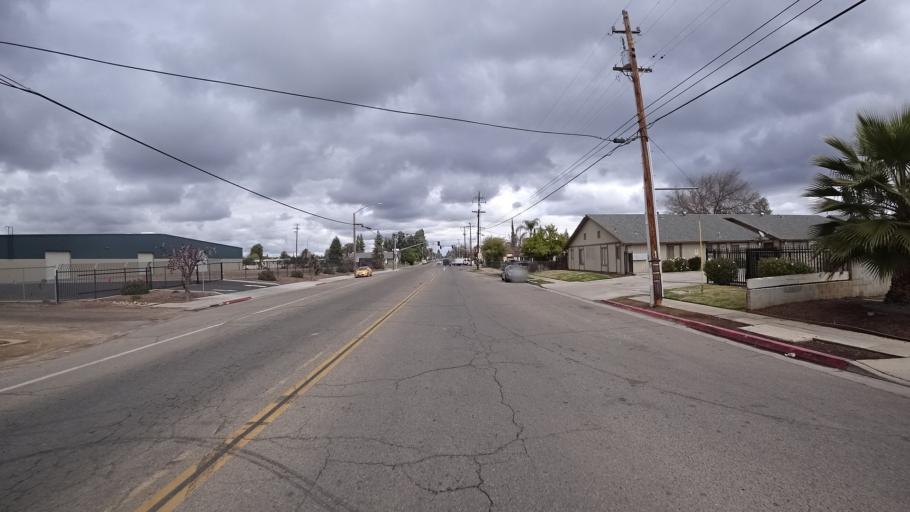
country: US
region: California
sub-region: Fresno County
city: West Park
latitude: 36.7854
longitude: -119.8444
